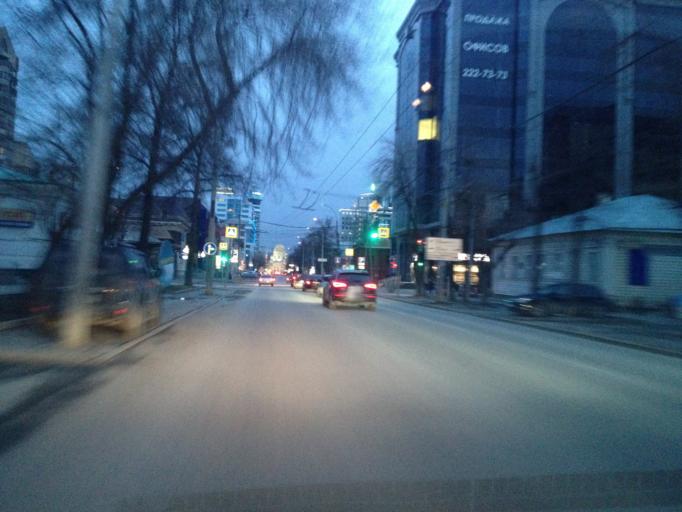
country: RU
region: Sverdlovsk
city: Yekaterinburg
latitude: 56.8337
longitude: 60.6125
